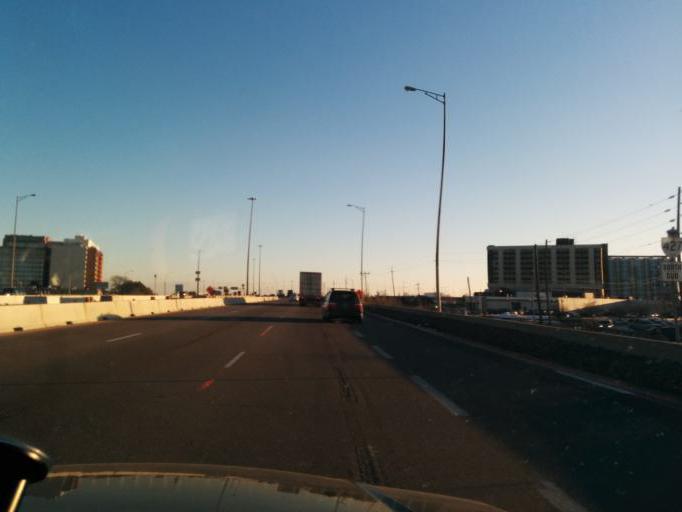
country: CA
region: Ontario
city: Etobicoke
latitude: 43.6903
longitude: -79.6038
